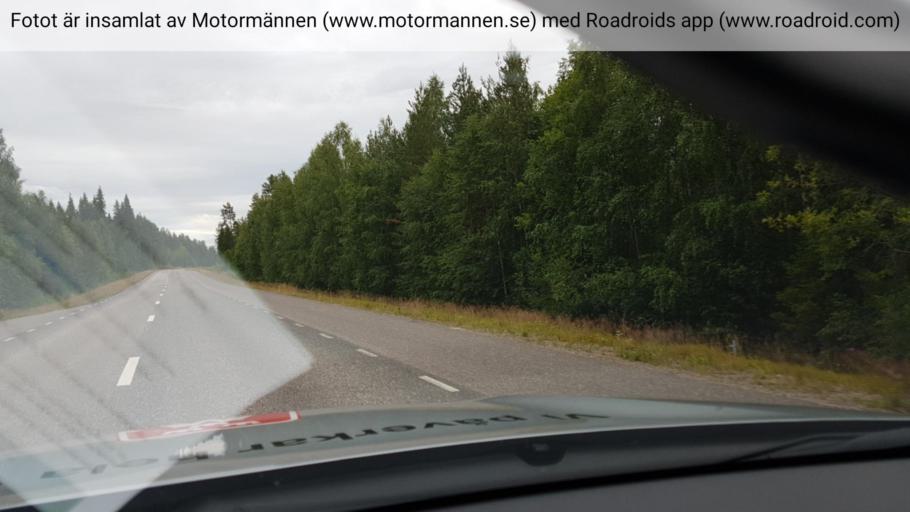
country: SE
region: Norrbotten
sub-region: Overkalix Kommun
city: OEverkalix
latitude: 66.5227
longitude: 22.7621
